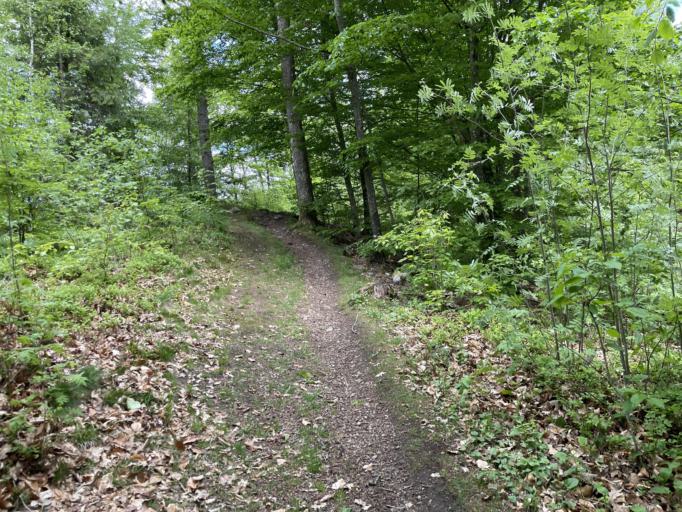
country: SE
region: Skane
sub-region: Klippans Kommun
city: Klippan
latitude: 56.1589
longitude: 13.1616
